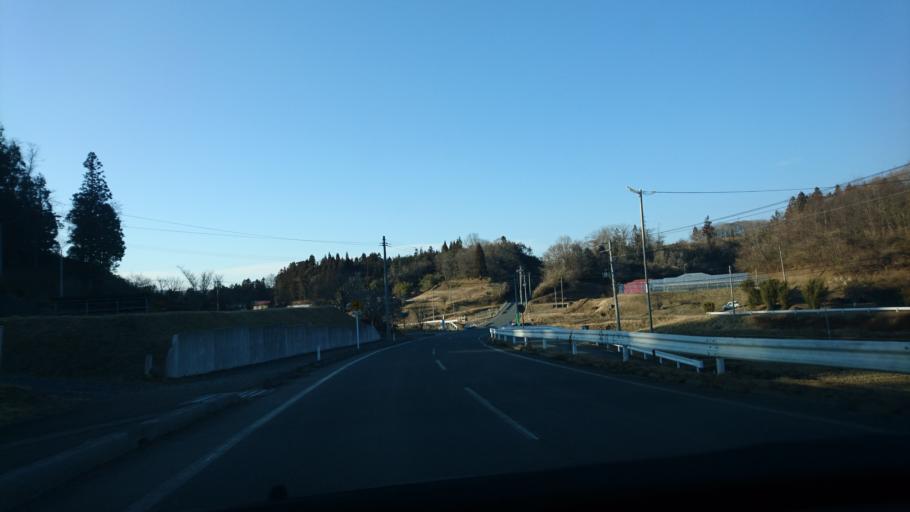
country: JP
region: Iwate
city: Ichinoseki
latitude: 38.9313
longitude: 141.3597
